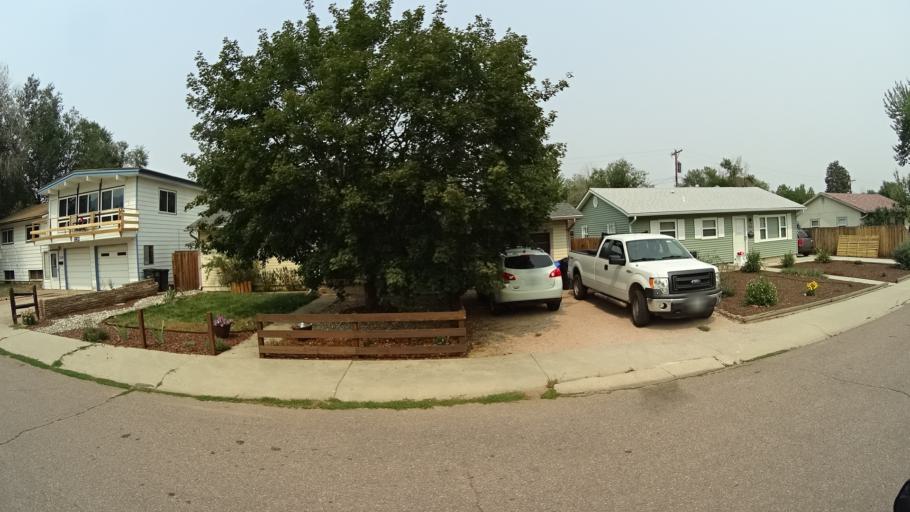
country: US
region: Colorado
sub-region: El Paso County
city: Stratmoor
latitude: 38.7975
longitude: -104.8077
